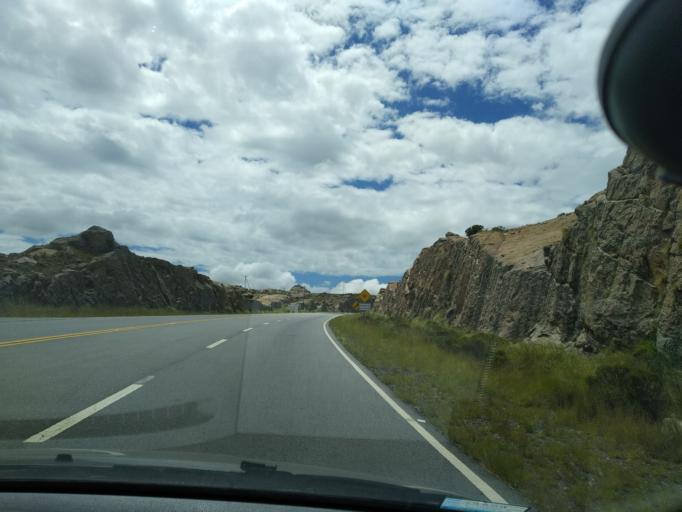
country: AR
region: Cordoba
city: Villa Cura Brochero
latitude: -31.6128
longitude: -64.9060
